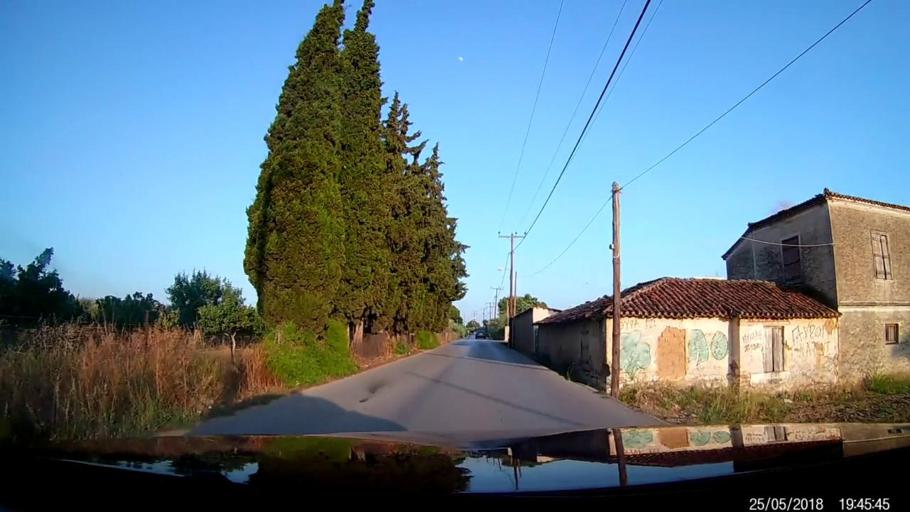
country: GR
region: Central Greece
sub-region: Nomos Evvoias
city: Ayios Nikolaos
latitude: 38.4305
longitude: 23.6352
